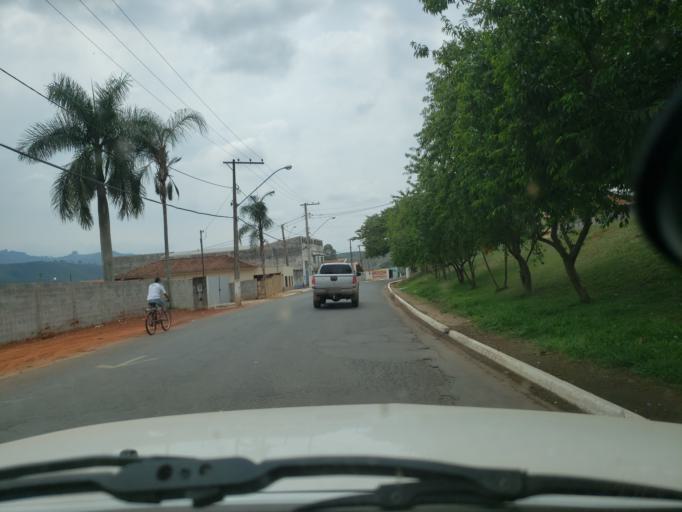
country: BR
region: Minas Gerais
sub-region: Jacutinga
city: Jacutinga
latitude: -22.2772
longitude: -46.6057
